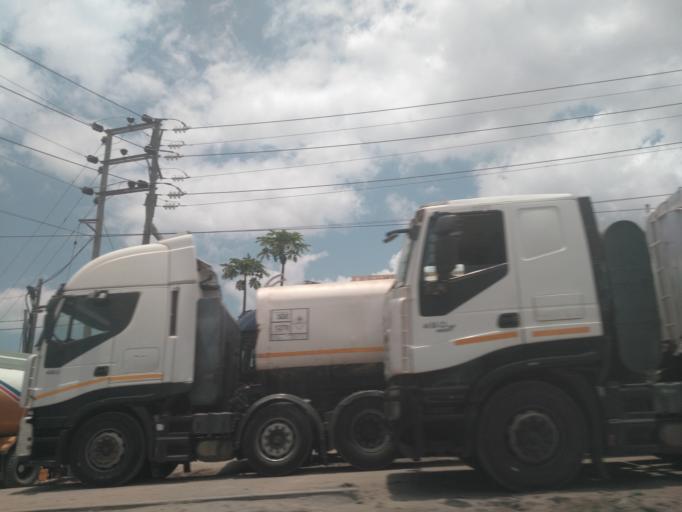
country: TZ
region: Dar es Salaam
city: Dar es Salaam
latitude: -6.8450
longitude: 39.2934
